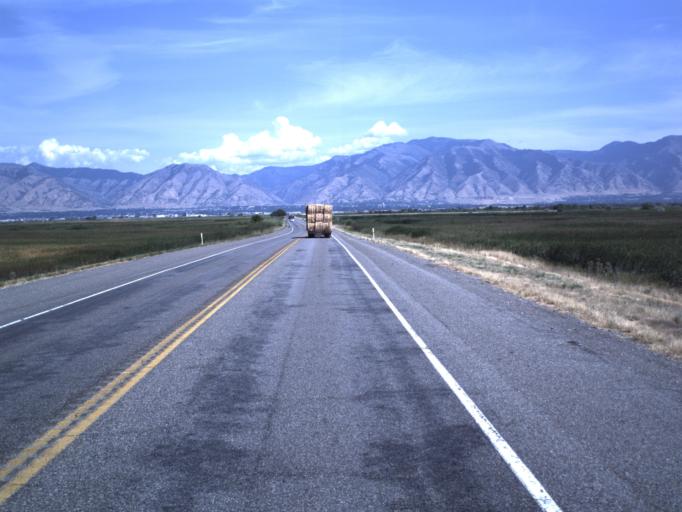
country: US
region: Utah
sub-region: Cache County
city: Mendon
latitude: 41.7461
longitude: -111.9507
